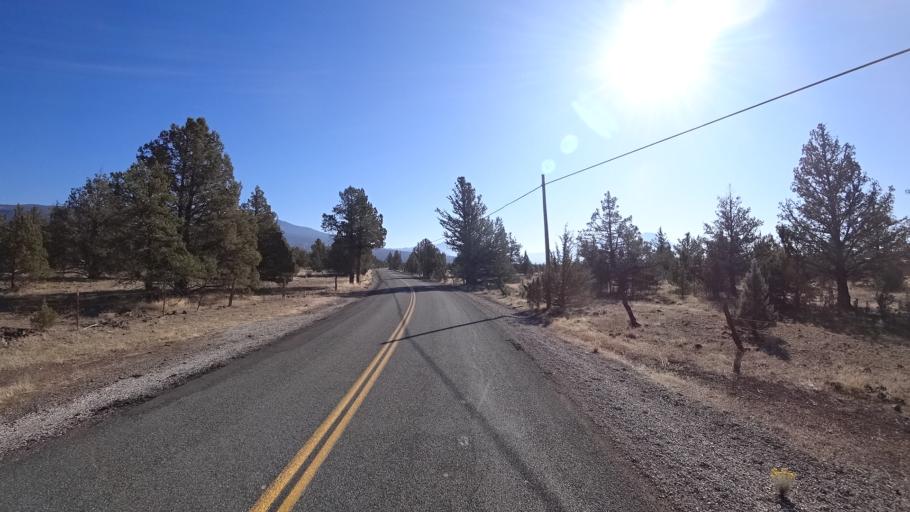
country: US
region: California
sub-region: Siskiyou County
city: Montague
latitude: 41.6465
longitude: -122.3586
